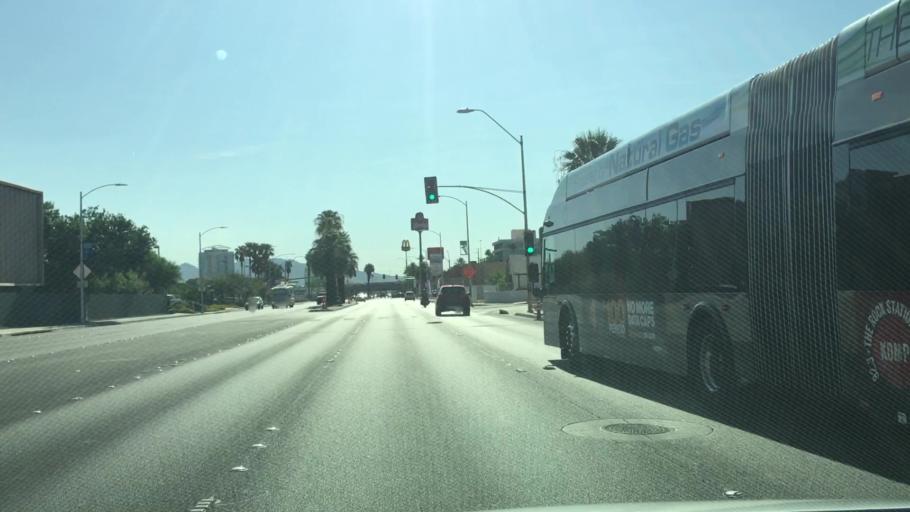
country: US
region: Nevada
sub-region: Clark County
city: Las Vegas
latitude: 36.1588
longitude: -115.1681
